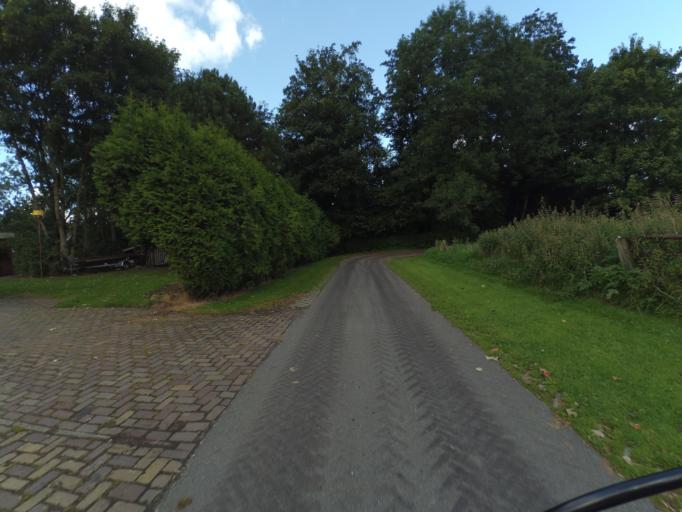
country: NL
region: Friesland
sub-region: Gemeente Dantumadiel
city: Broeksterwald
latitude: 53.2623
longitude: 6.0112
